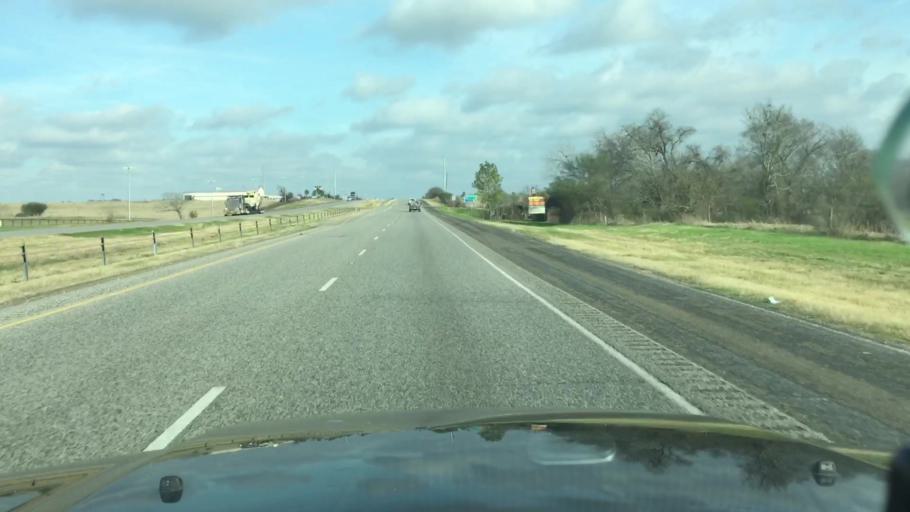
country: US
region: Texas
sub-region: Washington County
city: Brenham
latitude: 30.1366
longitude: -96.3330
